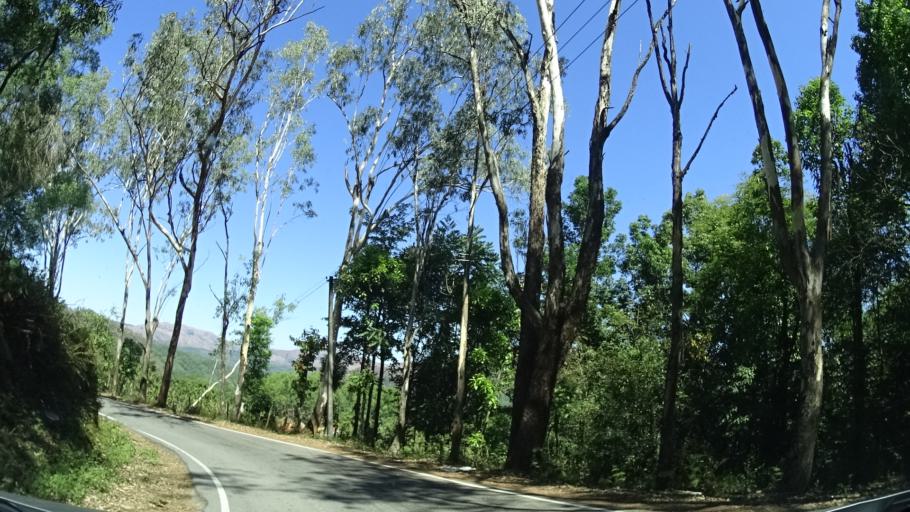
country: IN
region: Karnataka
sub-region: Chikmagalur
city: Sringeri
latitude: 13.1963
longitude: 75.2934
